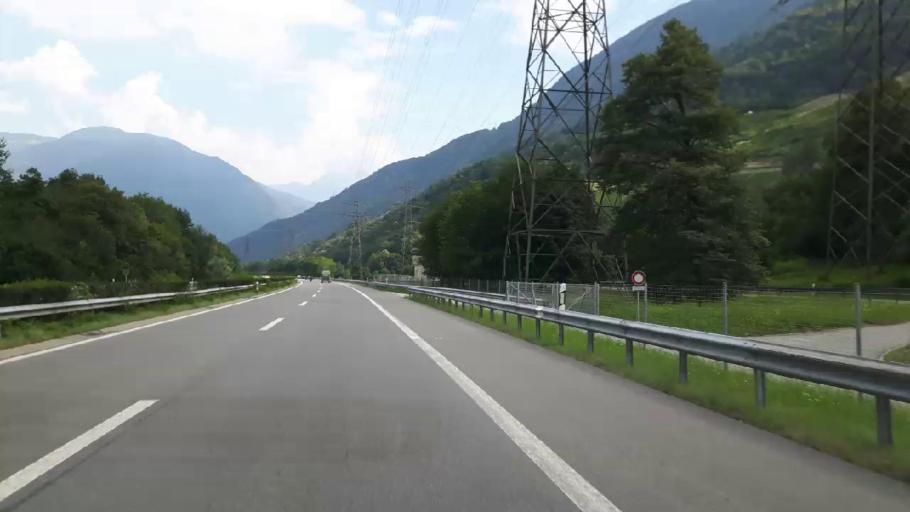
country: CH
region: Ticino
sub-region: Riviera District
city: Claro
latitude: 46.2508
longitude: 9.0105
